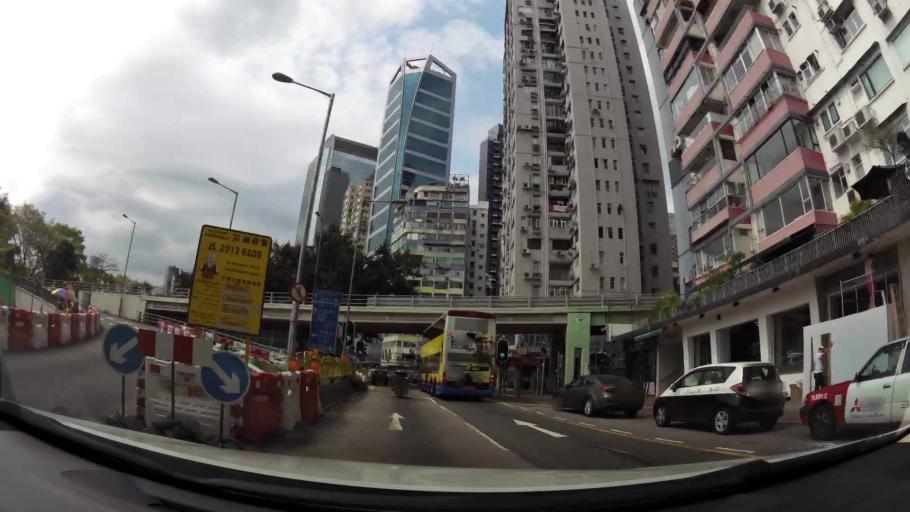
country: HK
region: Wanchai
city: Wan Chai
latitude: 22.2845
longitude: 114.1906
